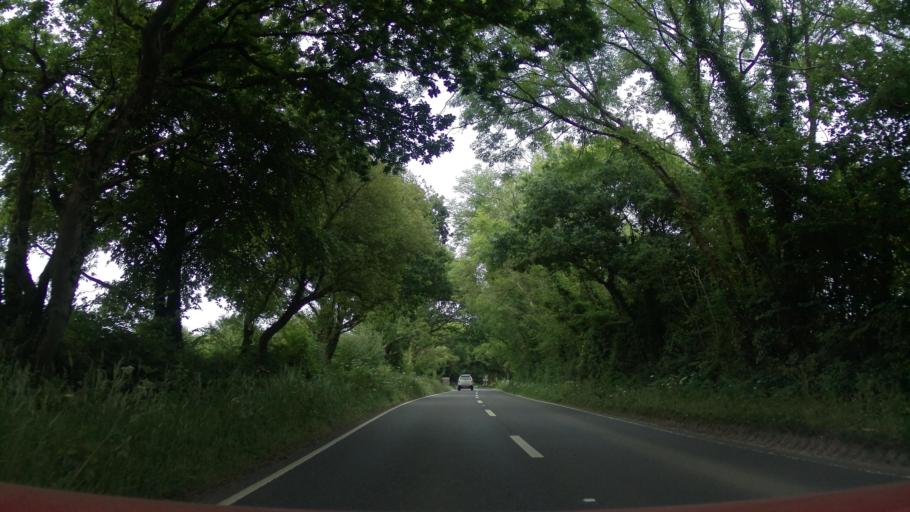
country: GB
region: England
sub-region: Devon
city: Sidmouth
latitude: 50.7046
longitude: -3.1830
